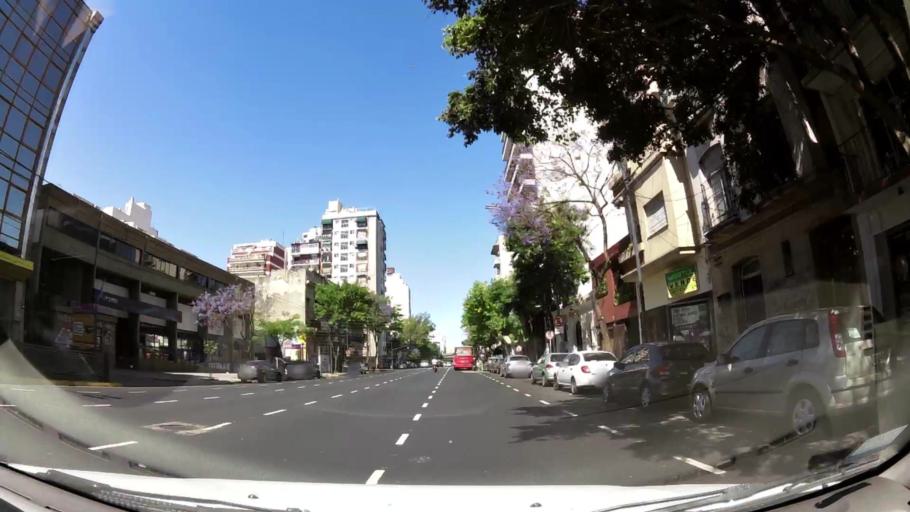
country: AR
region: Buenos Aires F.D.
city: Buenos Aires
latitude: -34.6224
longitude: -58.3853
